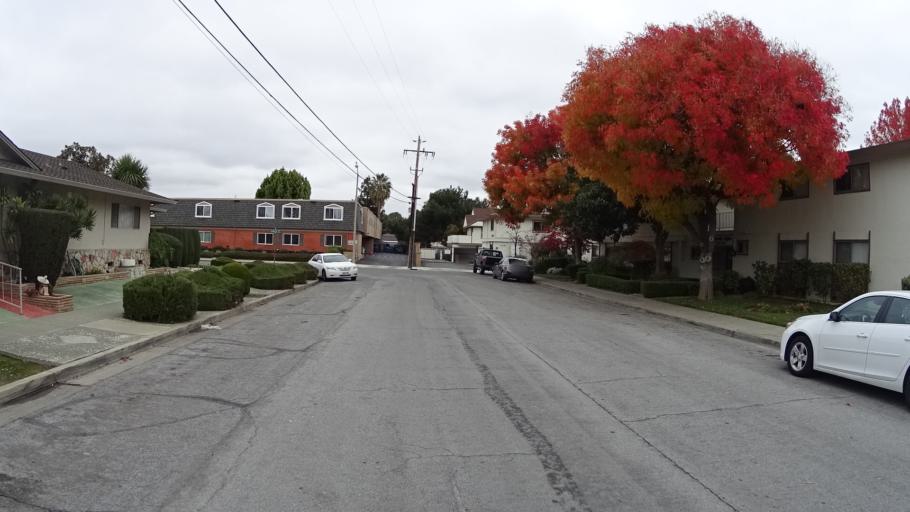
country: US
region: California
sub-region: Santa Clara County
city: Sunnyvale
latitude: 37.3618
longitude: -122.0284
